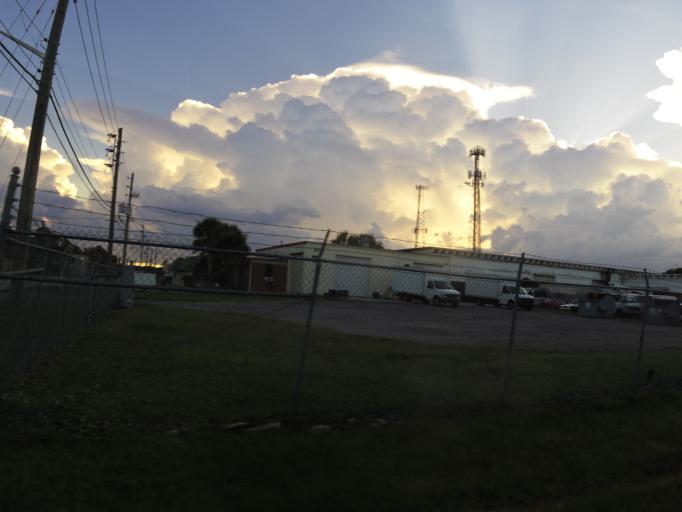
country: US
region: Florida
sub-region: Duval County
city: Jacksonville
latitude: 30.2607
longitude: -81.6092
